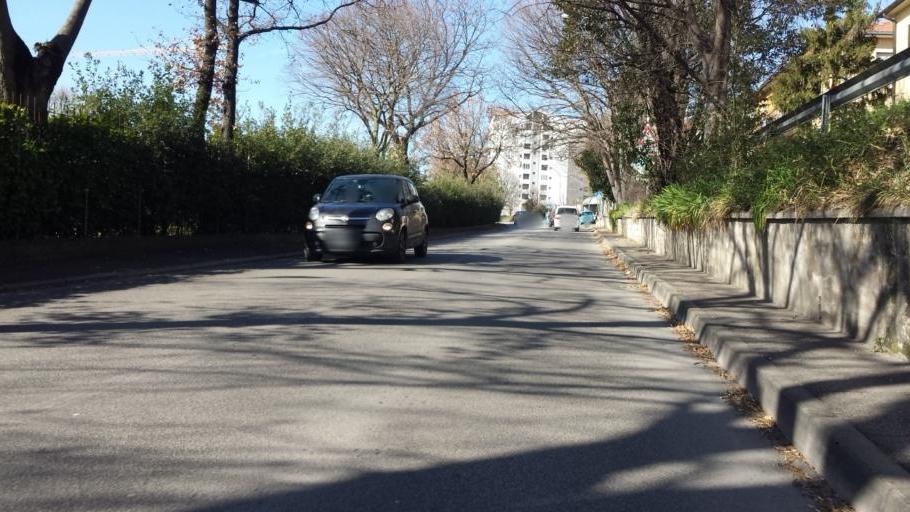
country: IT
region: Umbria
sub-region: Provincia di Terni
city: Terni
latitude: 42.5837
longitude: 12.6151
